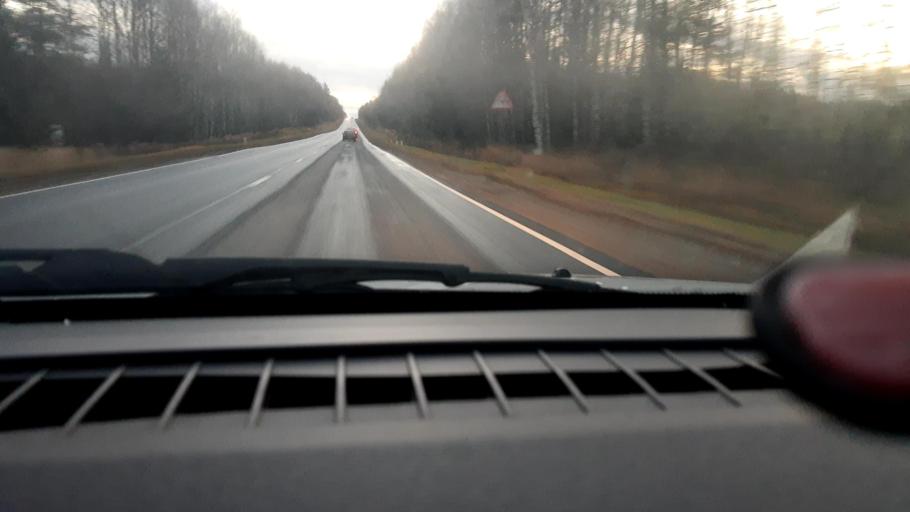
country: RU
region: Nizjnij Novgorod
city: Vladimirskoye
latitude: 56.9536
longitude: 45.0918
